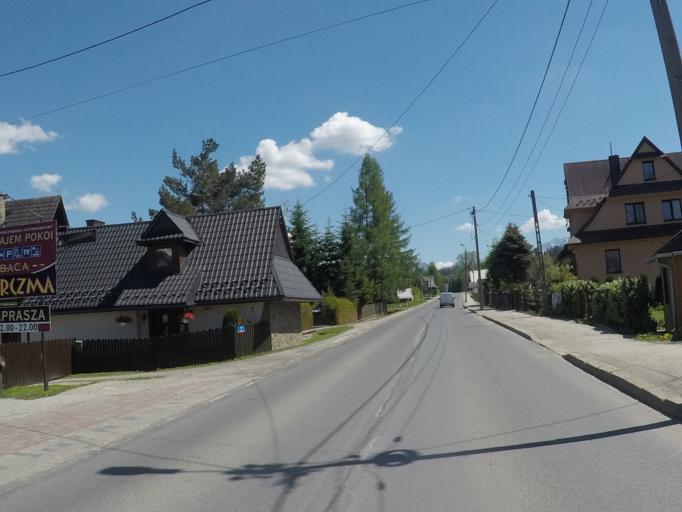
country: PL
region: Lesser Poland Voivodeship
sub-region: Powiat tatrzanski
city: Poronin
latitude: 49.3340
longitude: 20.0095
